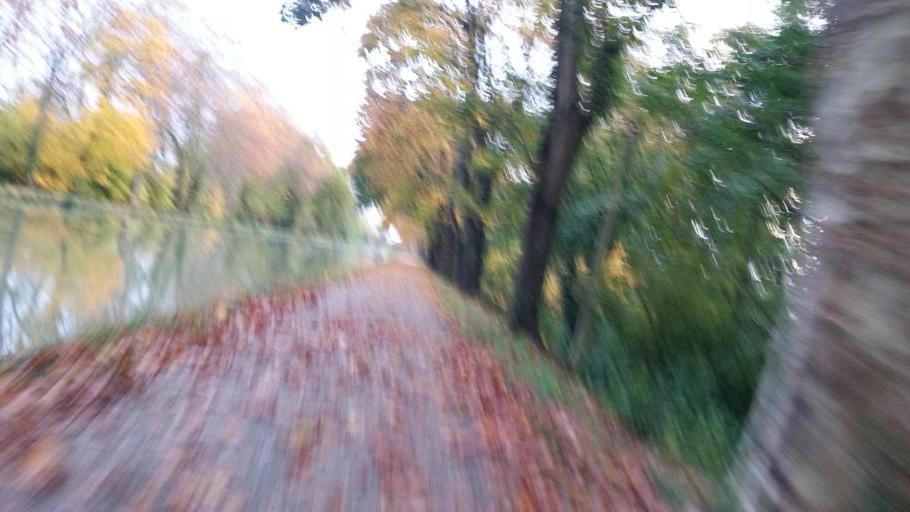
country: FR
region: Midi-Pyrenees
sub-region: Departement du Tarn-et-Garonne
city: Moissac
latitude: 44.0801
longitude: 1.0994
